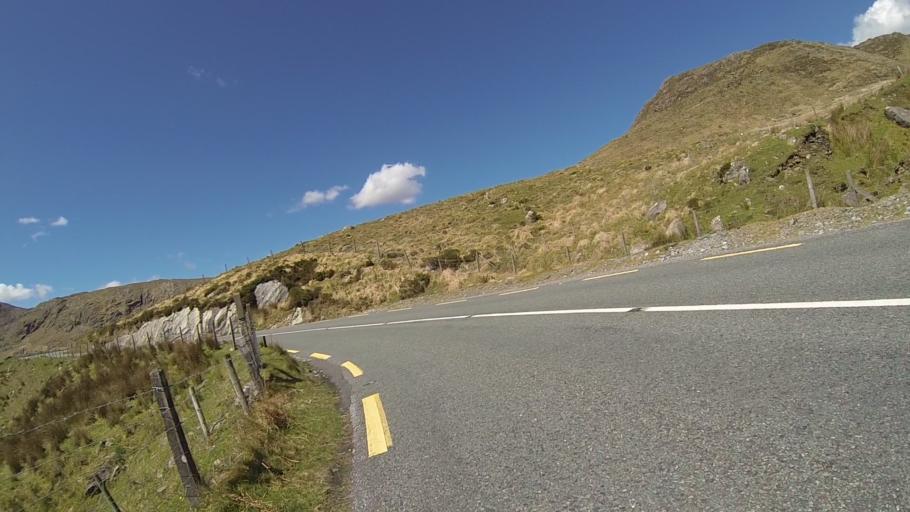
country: IE
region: Munster
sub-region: Ciarrai
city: Kenmare
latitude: 51.9311
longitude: -9.6467
